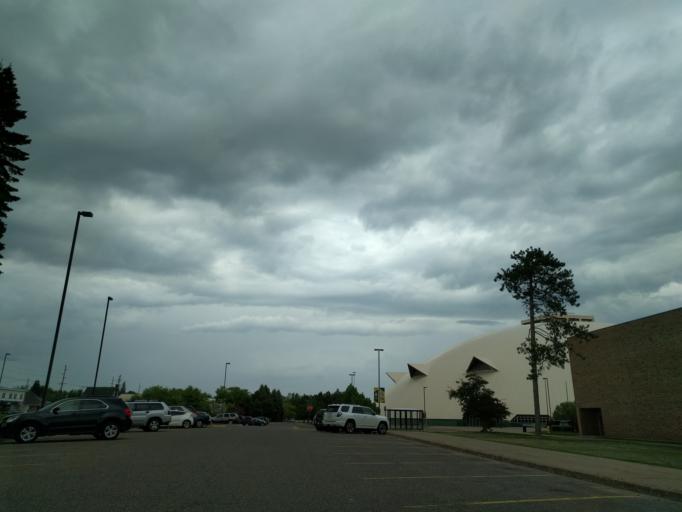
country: US
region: Michigan
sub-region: Marquette County
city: Marquette
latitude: 46.5585
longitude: -87.3953
